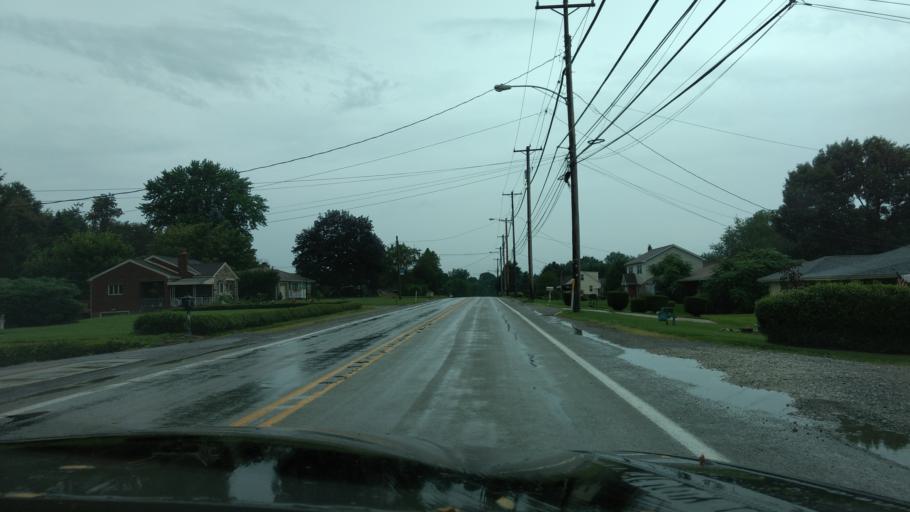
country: US
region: Pennsylvania
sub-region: Allegheny County
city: Emsworth
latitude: 40.5019
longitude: -80.1196
